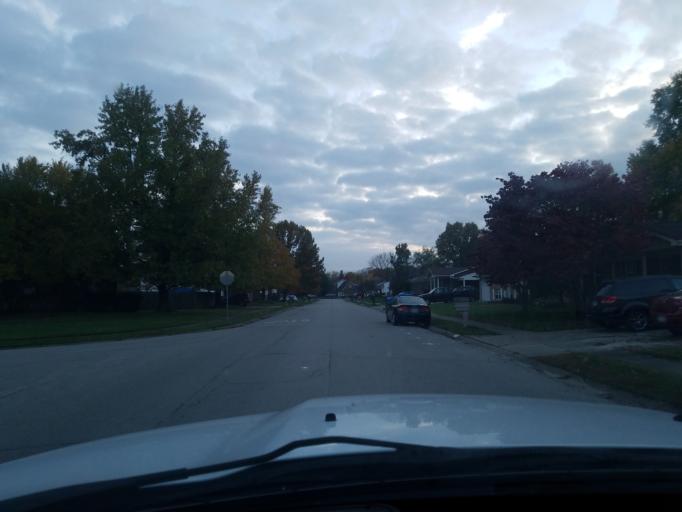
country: US
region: Indiana
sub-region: Floyd County
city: New Albany
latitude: 38.3490
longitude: -85.8101
